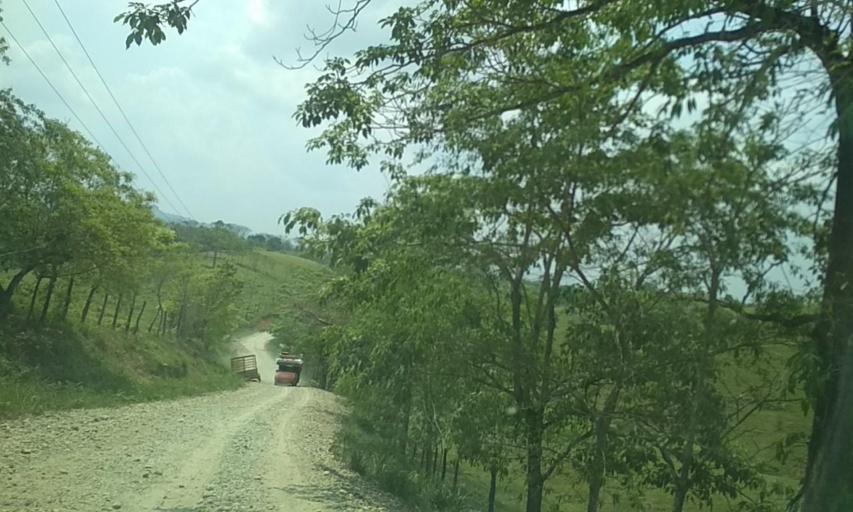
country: MX
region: Tabasco
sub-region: Huimanguillo
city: Francisco Rueda
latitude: 17.6216
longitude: -93.8160
